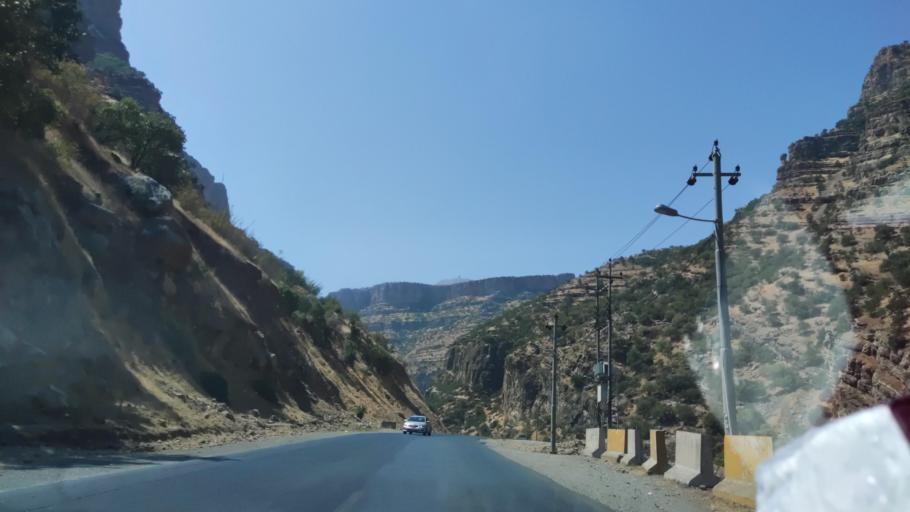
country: IQ
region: Arbil
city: Ruwandiz
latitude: 36.6423
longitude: 44.4933
